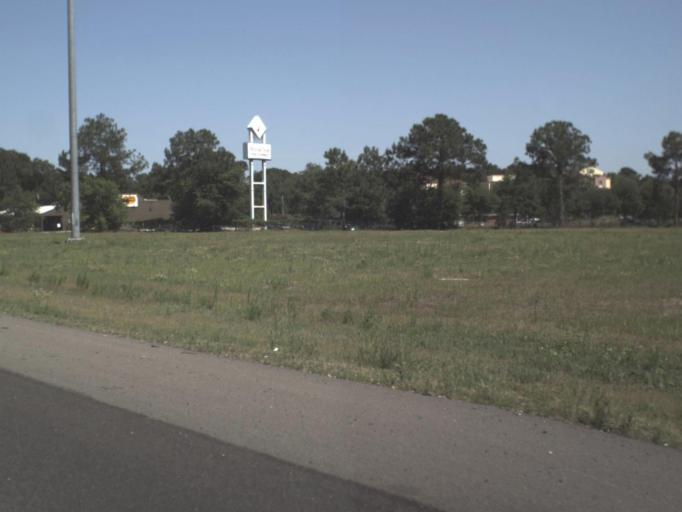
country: US
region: Florida
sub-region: Duval County
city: Baldwin
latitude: 30.3091
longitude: -81.8467
